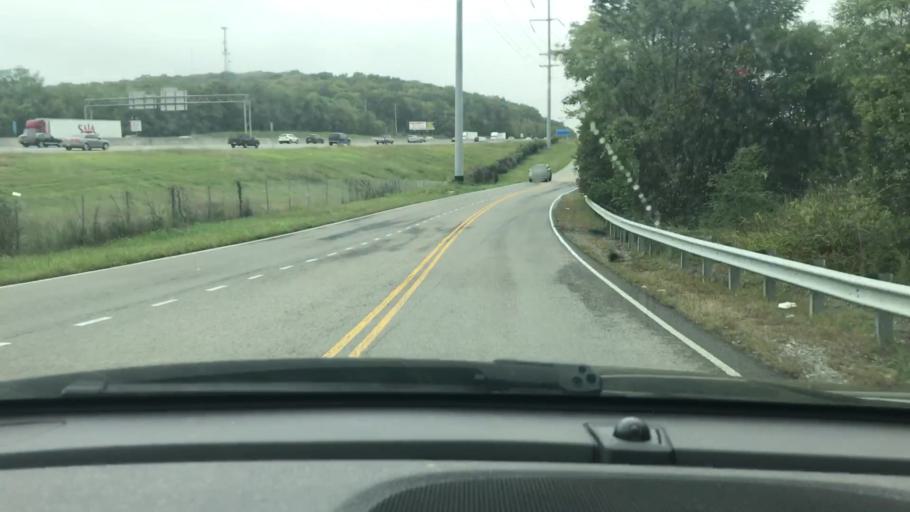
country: US
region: Tennessee
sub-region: Rutherford County
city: La Vergne
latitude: 35.9784
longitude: -86.5733
